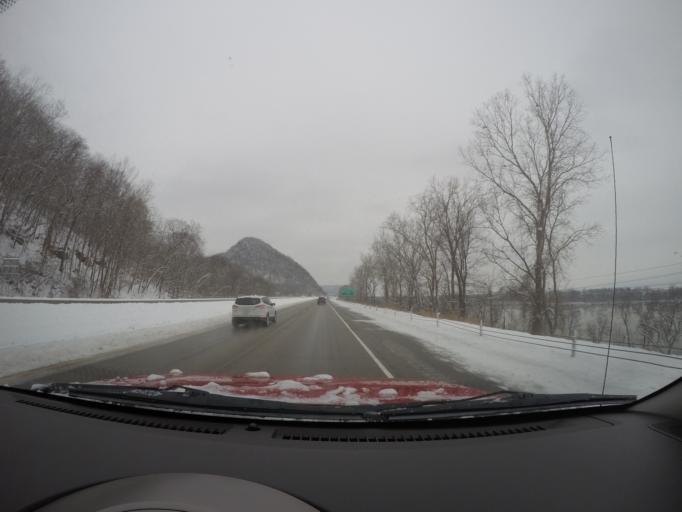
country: US
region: Minnesota
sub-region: Houston County
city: La Crescent
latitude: 43.8725
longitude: -91.3191
